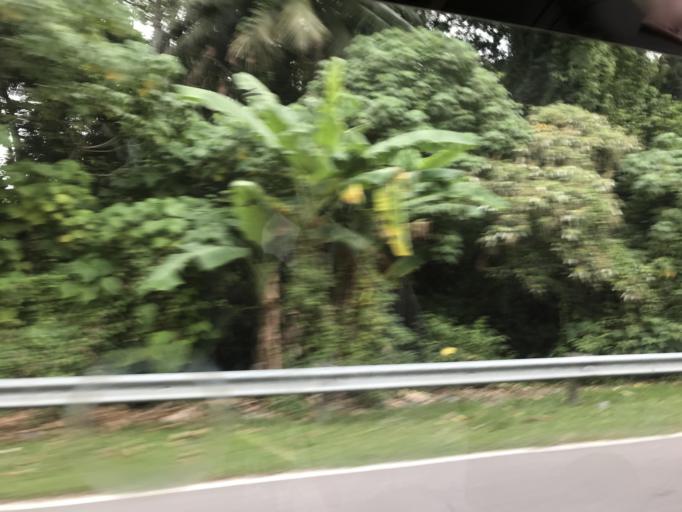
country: MY
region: Kelantan
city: Kota Bharu
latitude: 6.1503
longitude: 102.2288
